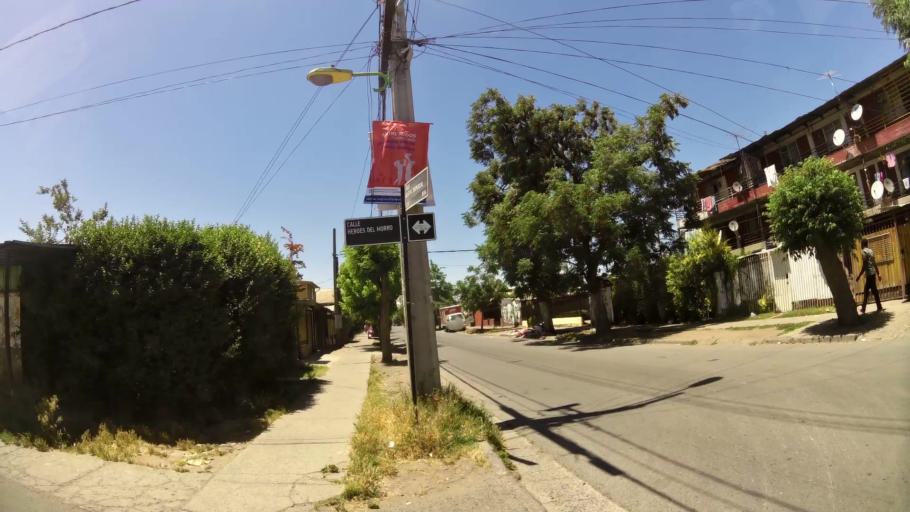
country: CL
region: Santiago Metropolitan
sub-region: Provincia de Maipo
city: San Bernardo
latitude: -33.5759
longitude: -70.6699
